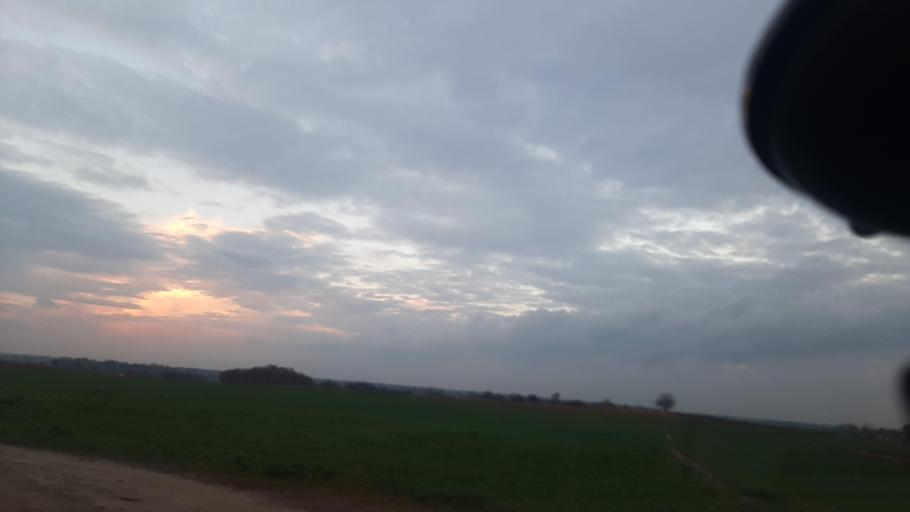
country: PL
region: Lublin Voivodeship
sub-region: Powiat lubelski
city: Jastkow
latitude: 51.3322
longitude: 22.3937
